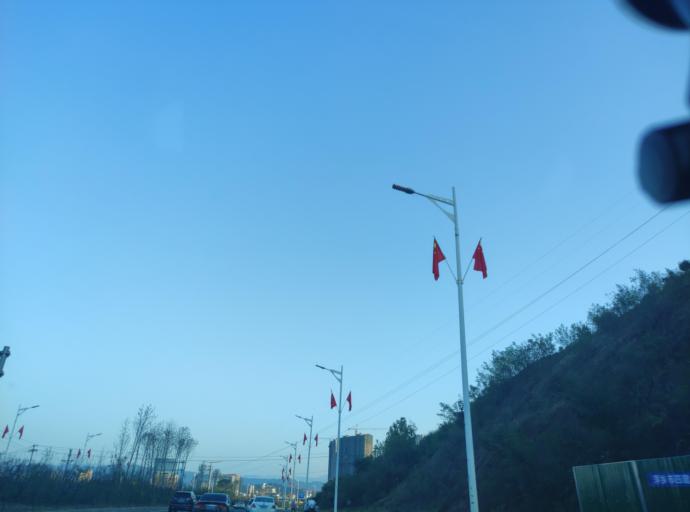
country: CN
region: Jiangxi Sheng
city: Pingxiang
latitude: 27.6424
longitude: 113.8270
